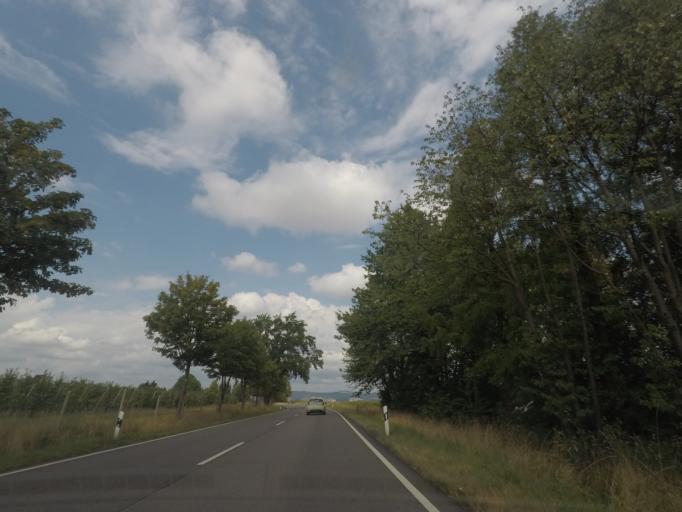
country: DE
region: Saxony
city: Pirna
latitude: 50.9356
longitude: 13.9690
